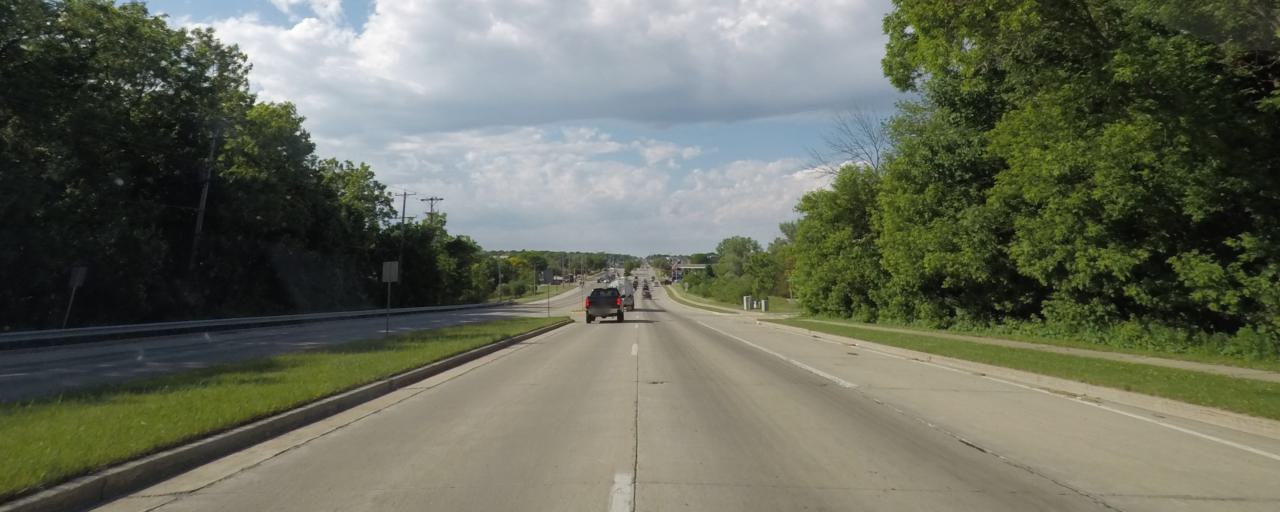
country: US
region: Wisconsin
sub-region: Milwaukee County
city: Greendale
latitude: 42.9422
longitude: -88.0085
